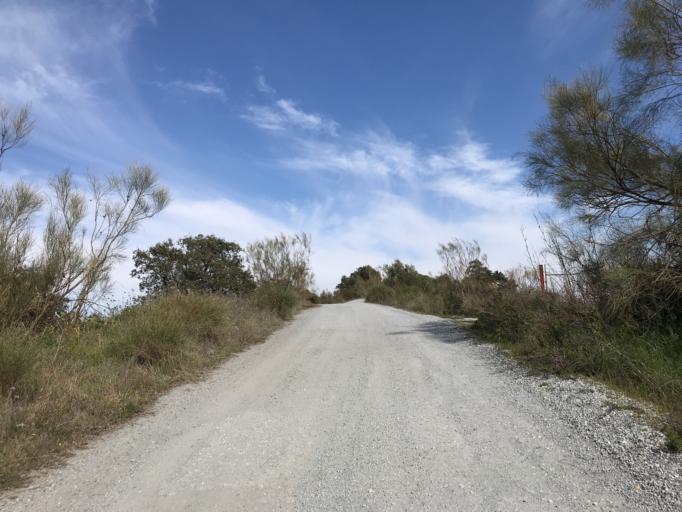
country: ES
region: Andalusia
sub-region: Provincia de Malaga
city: Valdes
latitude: 36.7812
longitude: -4.2252
